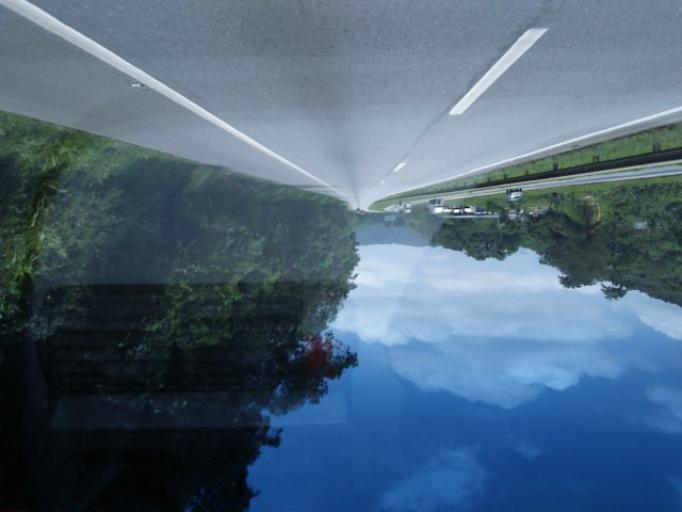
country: BR
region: Sao Paulo
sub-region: Miracatu
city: Miracatu
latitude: -24.1959
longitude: -47.3640
